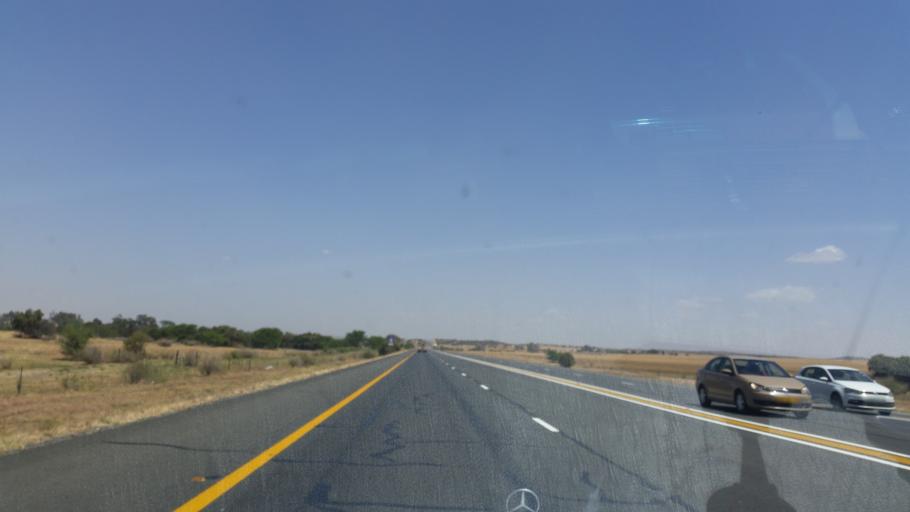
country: ZA
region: Orange Free State
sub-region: Lejweleputswa District Municipality
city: Brandfort
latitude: -28.8937
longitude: 26.4789
